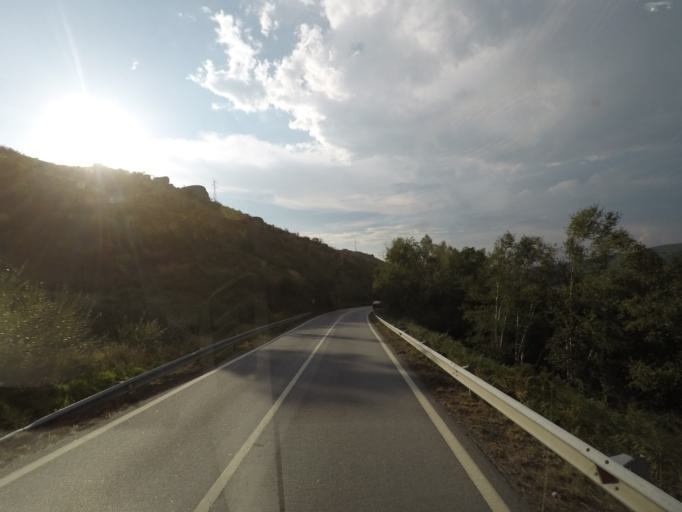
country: PT
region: Porto
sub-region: Baiao
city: Valadares
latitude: 41.1983
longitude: -7.9527
